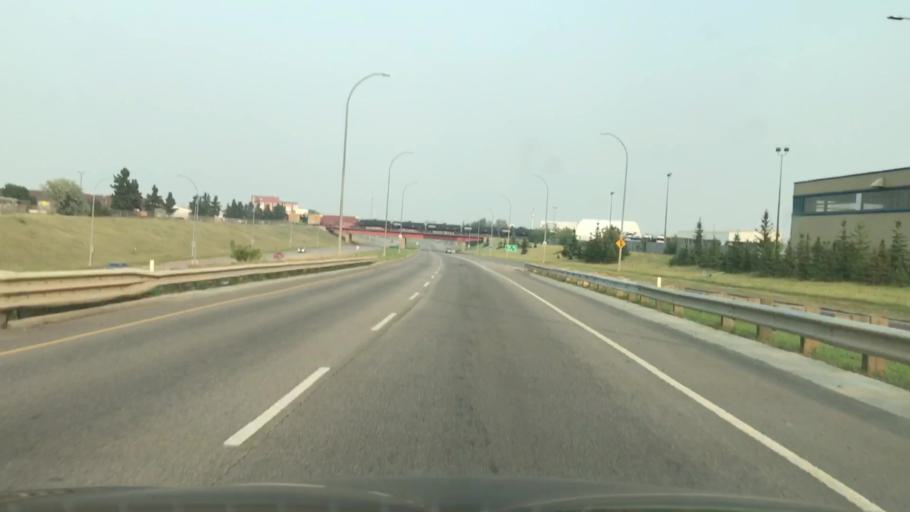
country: CA
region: Alberta
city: Edmonton
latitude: 53.5157
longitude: -113.4304
